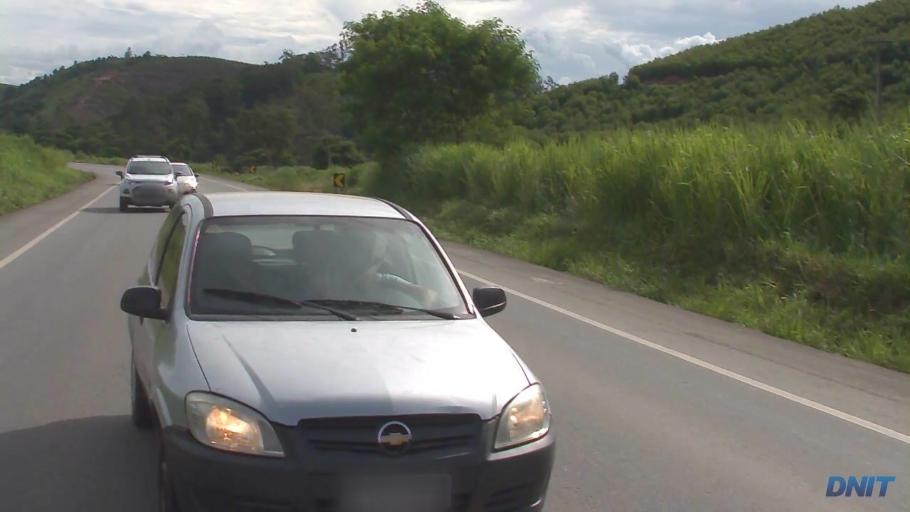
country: BR
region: Minas Gerais
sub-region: Belo Oriente
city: Belo Oriente
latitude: -19.2721
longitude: -42.3567
